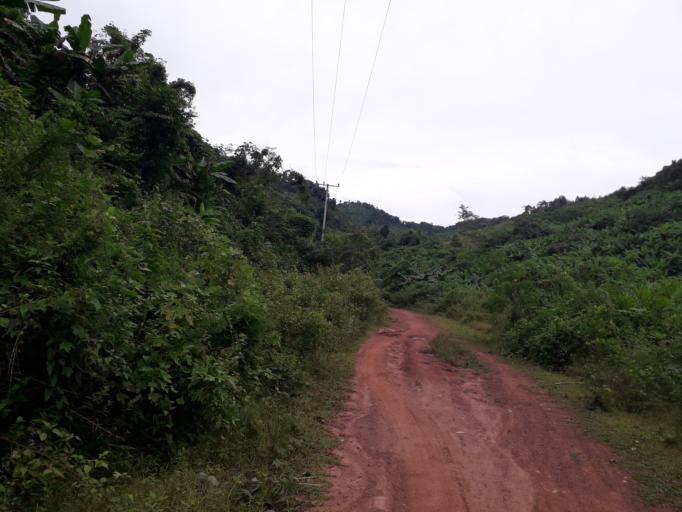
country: CN
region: Yunnan
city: Menglie
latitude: 22.1903
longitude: 101.7063
